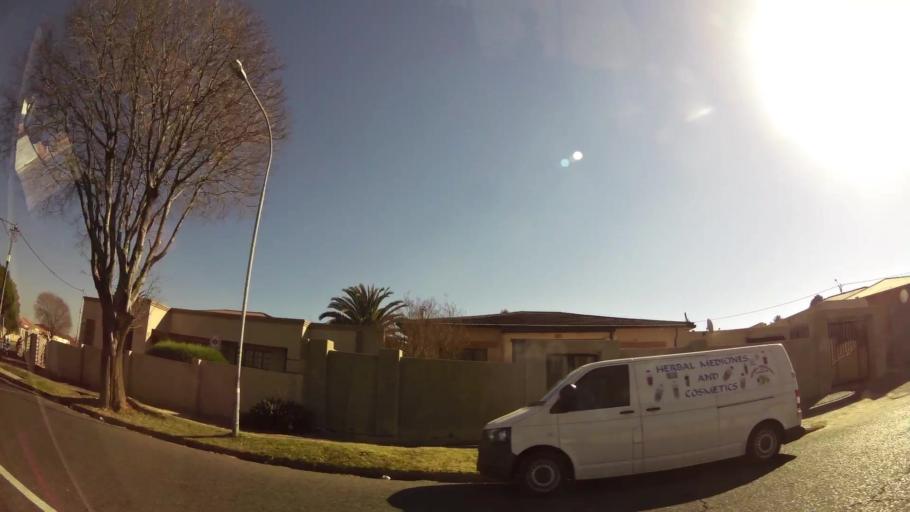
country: ZA
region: Gauteng
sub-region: City of Johannesburg Metropolitan Municipality
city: Johannesburg
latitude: -26.1936
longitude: 27.9890
